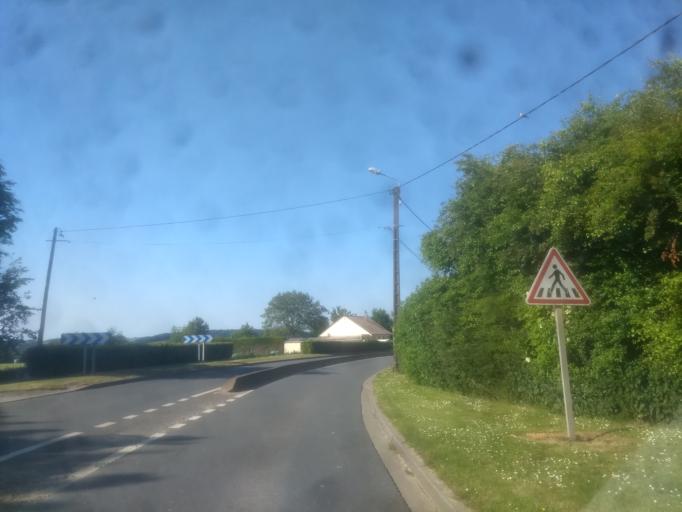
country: FR
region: Picardie
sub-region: Departement de la Somme
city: Doullens
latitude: 50.1547
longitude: 2.2851
